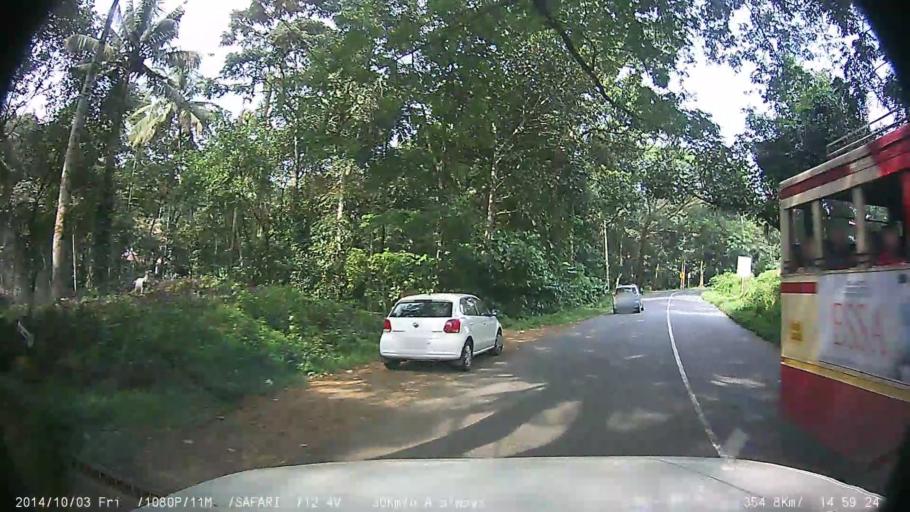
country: IN
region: Kerala
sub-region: Kottayam
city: Palackattumala
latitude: 9.8119
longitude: 76.5774
